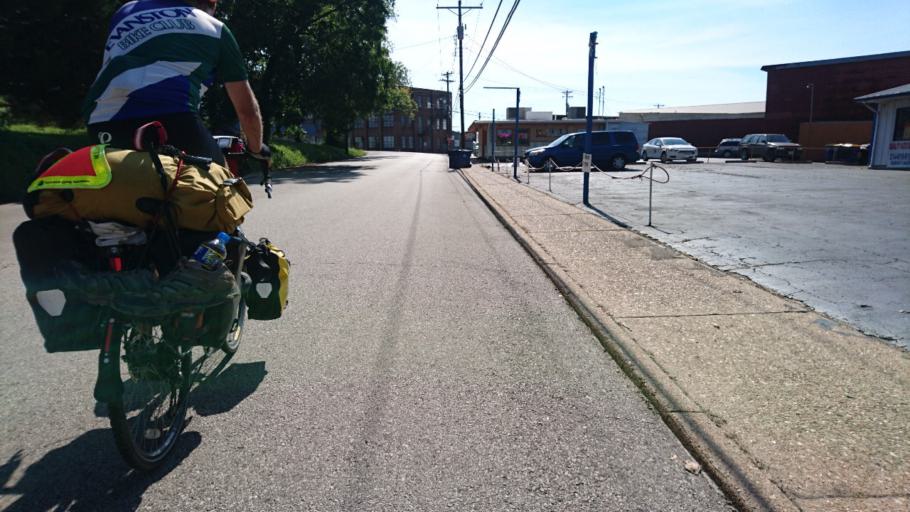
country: US
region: Missouri
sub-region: Franklin County
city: Saint Clair
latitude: 38.3496
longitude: -90.9815
